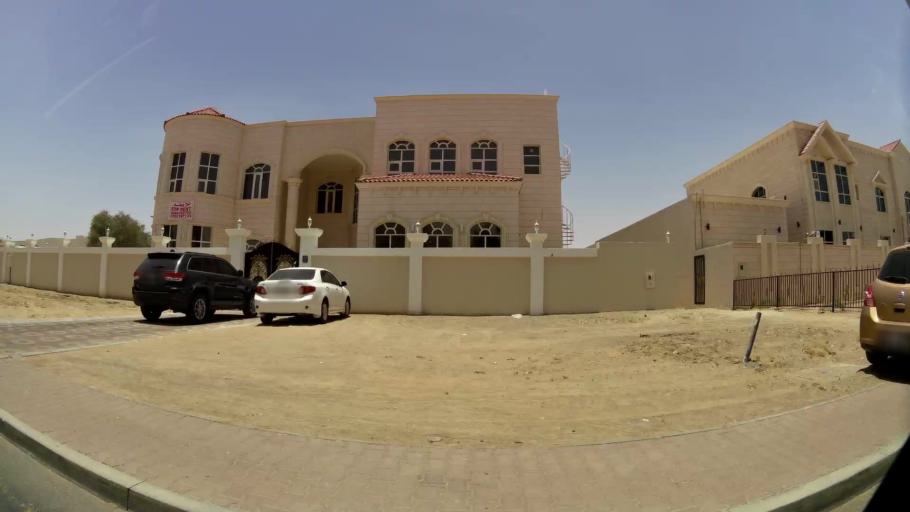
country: OM
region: Al Buraimi
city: Al Buraymi
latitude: 24.2618
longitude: 55.7361
